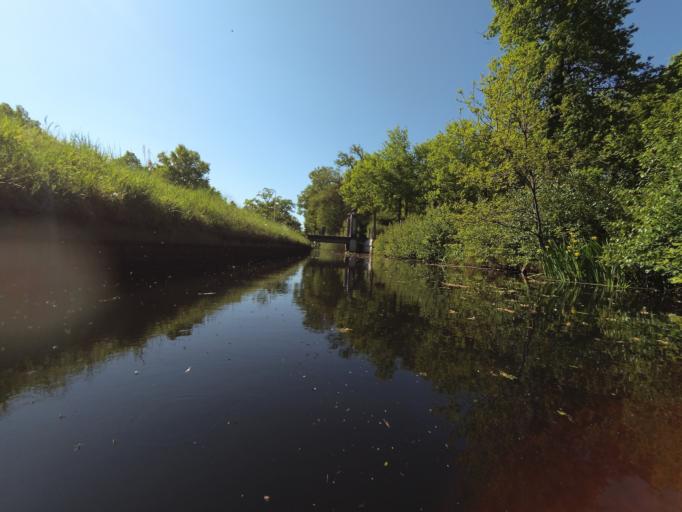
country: NL
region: Utrecht
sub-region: Gemeente Woudenberg
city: Woudenberg
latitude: 52.0992
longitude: 5.4176
